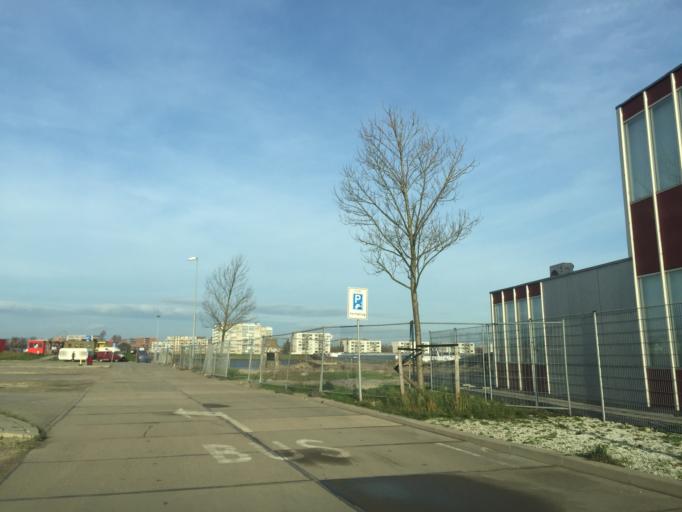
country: NL
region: South Holland
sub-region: Gemeente Papendrecht
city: Papendrecht
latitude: 51.8183
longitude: 4.6876
